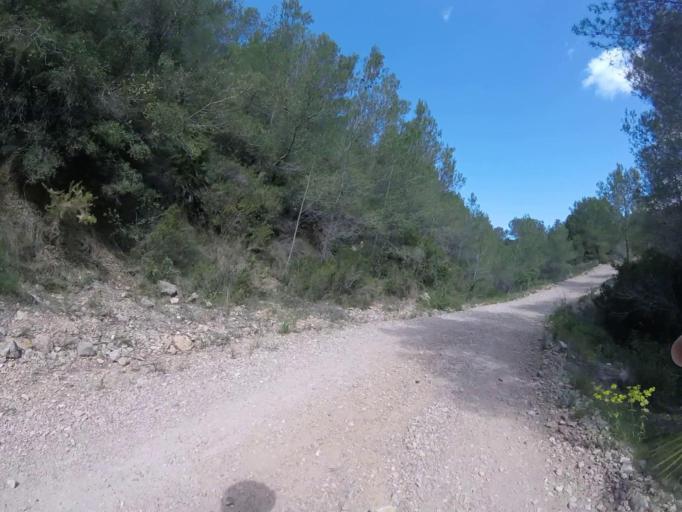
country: ES
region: Valencia
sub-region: Provincia de Castello
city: Alcoceber
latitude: 40.3000
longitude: 0.3150
